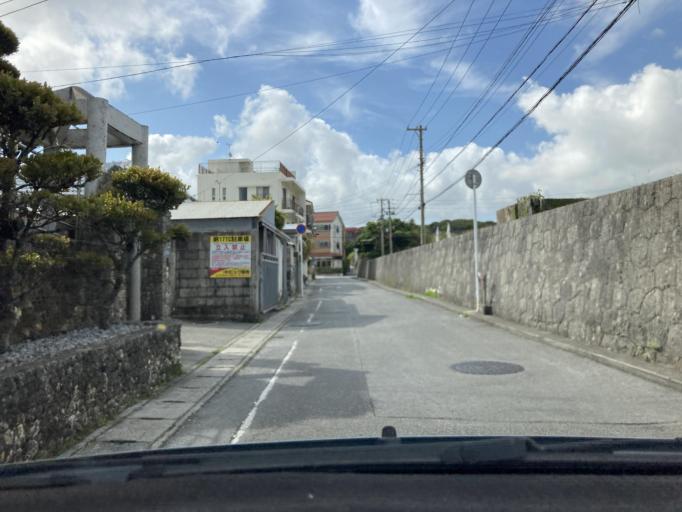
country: JP
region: Okinawa
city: Naha-shi
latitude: 26.2211
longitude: 127.7181
